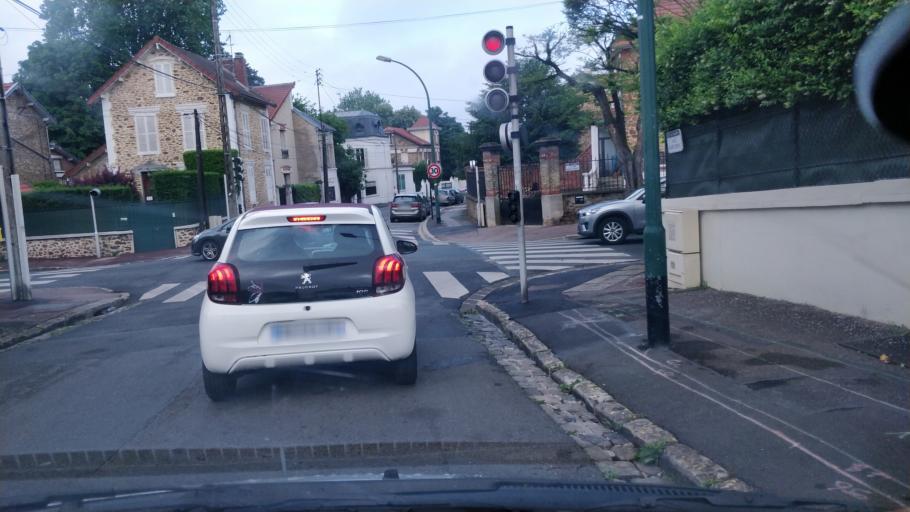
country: FR
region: Ile-de-France
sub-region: Departement de Seine-Saint-Denis
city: Le Raincy
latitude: 48.8978
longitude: 2.5131
